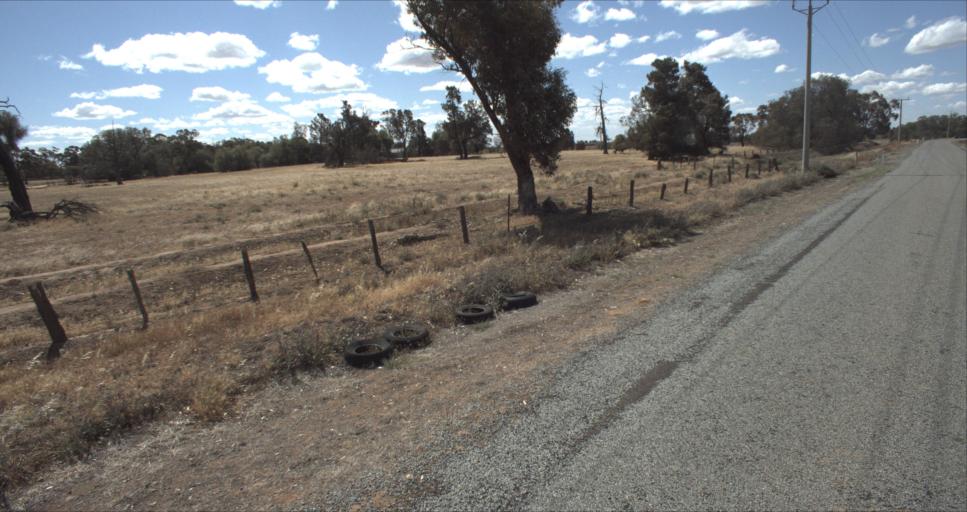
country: AU
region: New South Wales
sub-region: Leeton
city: Leeton
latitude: -34.5204
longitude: 146.2243
